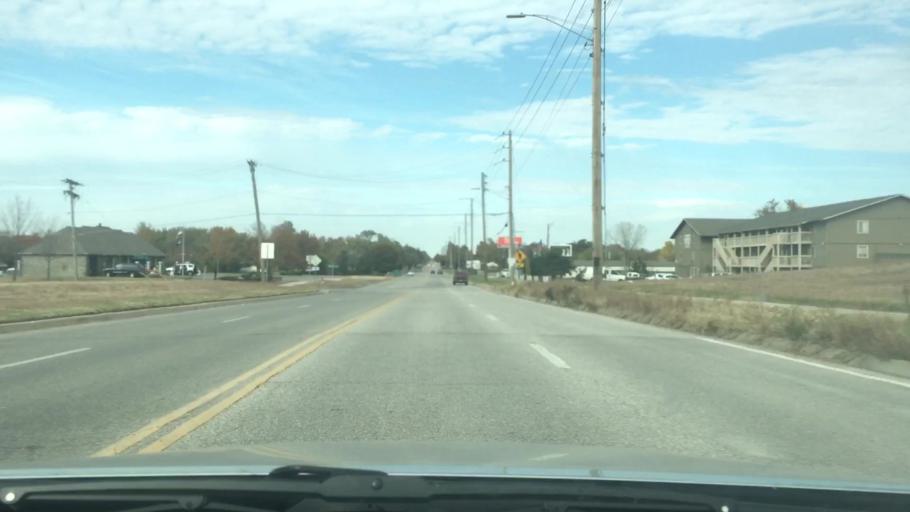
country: US
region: Kansas
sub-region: Sedgwick County
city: Wichita
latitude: 37.6566
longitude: -97.2621
